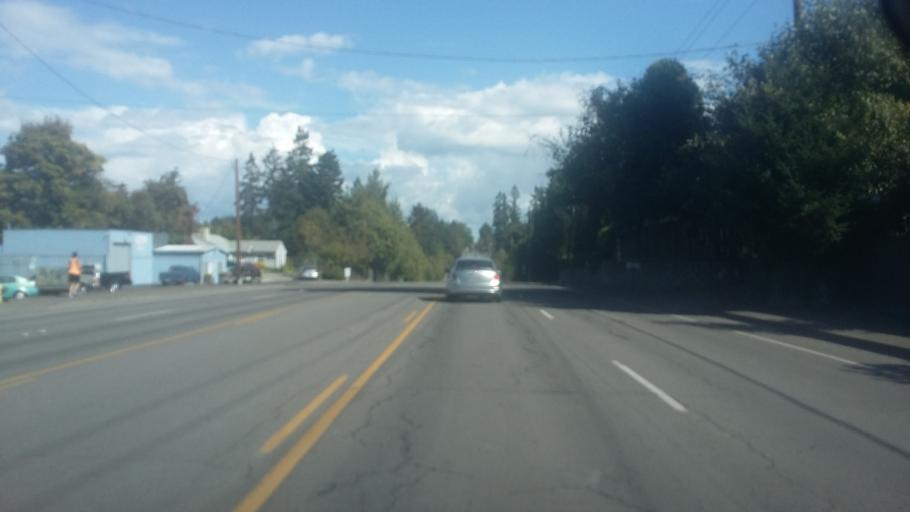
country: US
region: Washington
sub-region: Clark County
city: Salmon Creek
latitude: 45.6930
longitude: -122.6544
